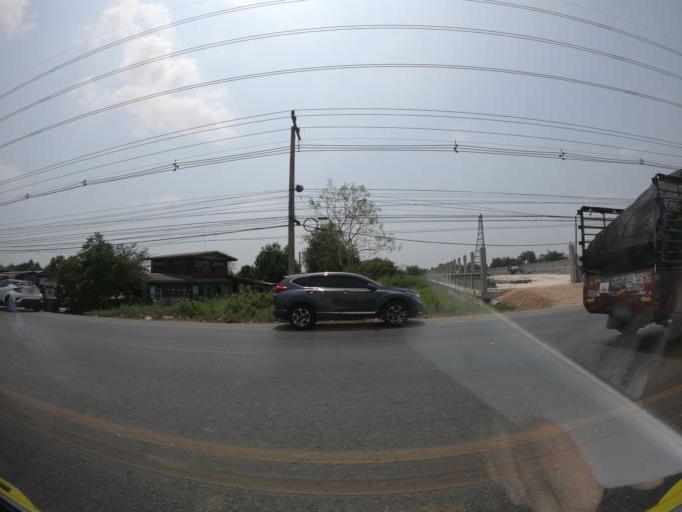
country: TH
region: Pathum Thani
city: Ban Lam Luk Ka
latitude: 13.9500
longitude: 100.8066
